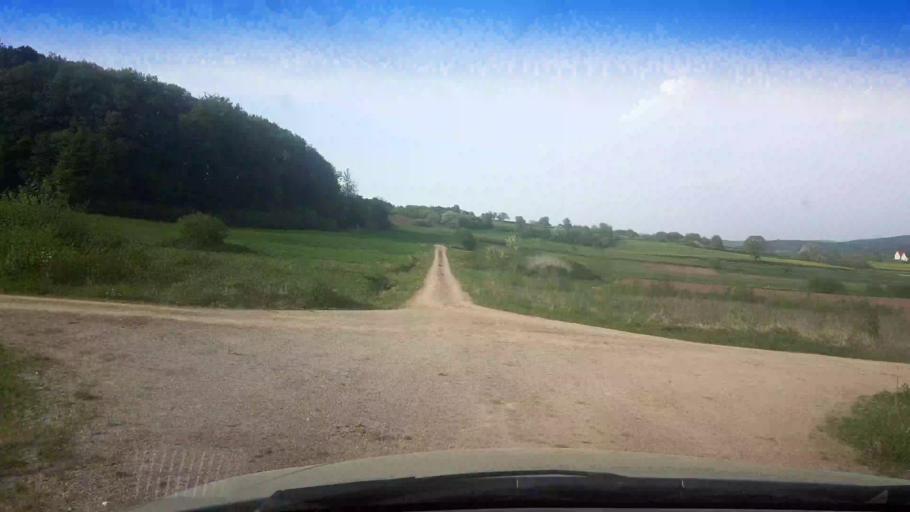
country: DE
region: Bavaria
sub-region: Upper Franconia
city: Rattelsdorf
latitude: 50.0137
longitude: 10.8682
